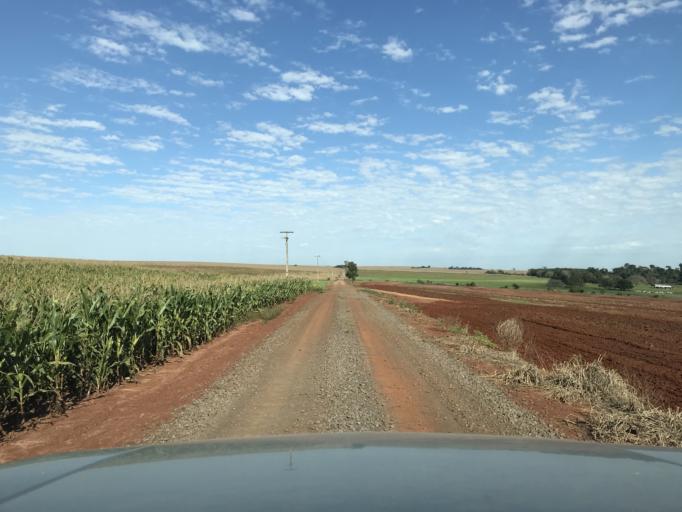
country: BR
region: Parana
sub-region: Palotina
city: Palotina
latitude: -24.1622
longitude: -53.7478
